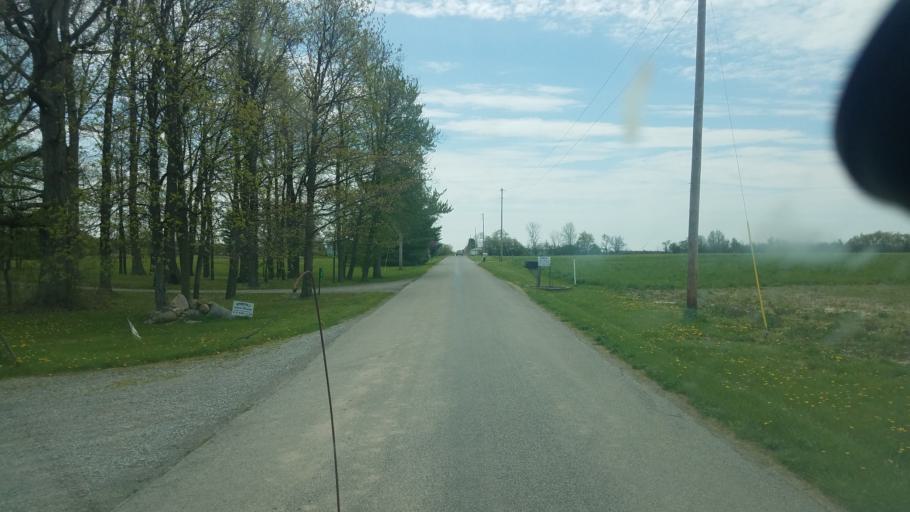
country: US
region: Ohio
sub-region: Hardin County
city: Ada
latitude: 40.8007
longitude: -83.9086
